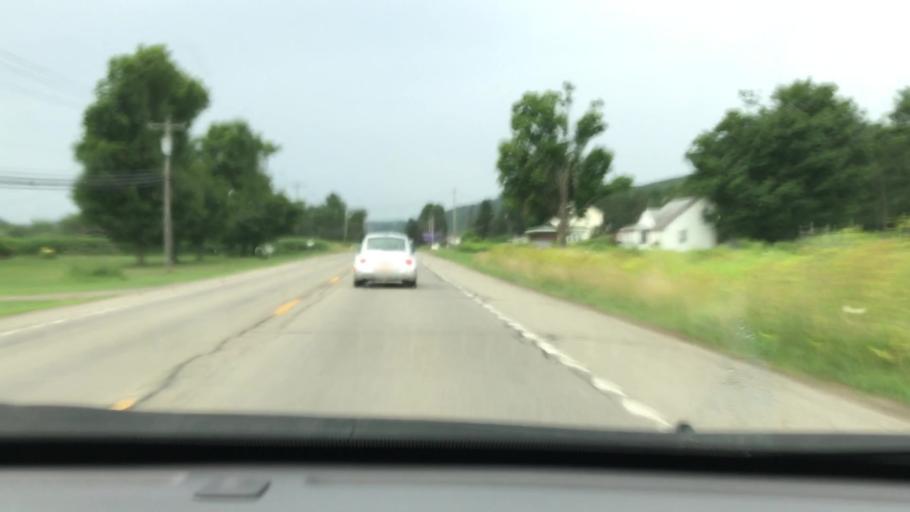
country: US
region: New York
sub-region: Cattaraugus County
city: Salamanca
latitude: 42.2011
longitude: -78.6480
